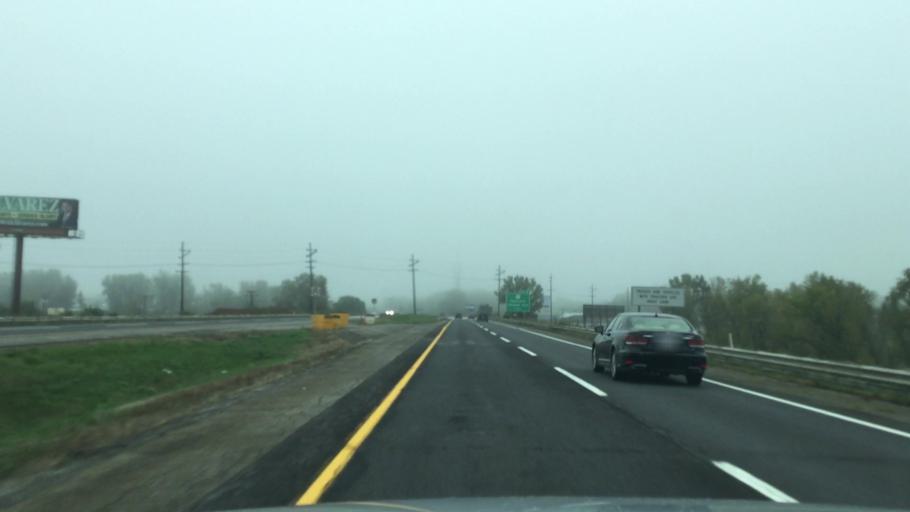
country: US
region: Indiana
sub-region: Lake County
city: Whiting
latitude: 41.6555
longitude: -87.5157
